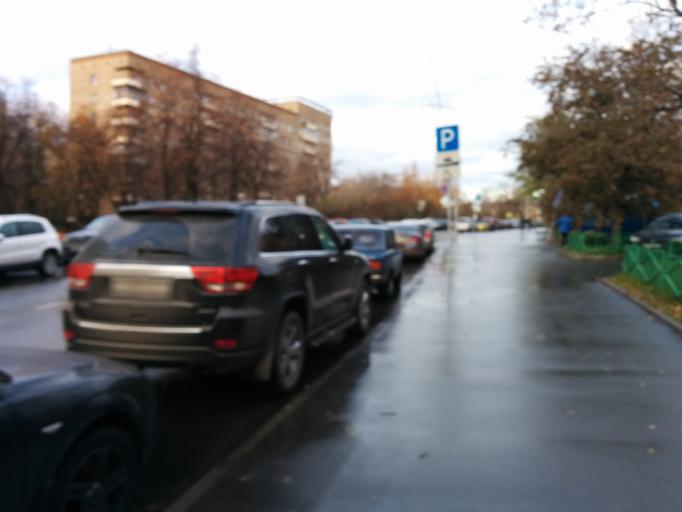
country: RU
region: Moscow
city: Novyye Cheremushki
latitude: 55.7272
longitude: 37.5858
